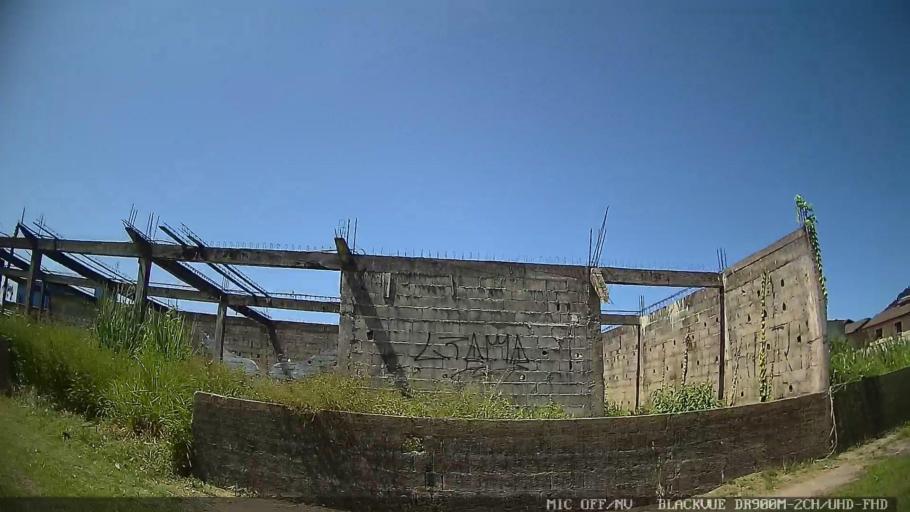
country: BR
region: Sao Paulo
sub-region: Peruibe
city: Peruibe
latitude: -24.3313
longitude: -47.0052
